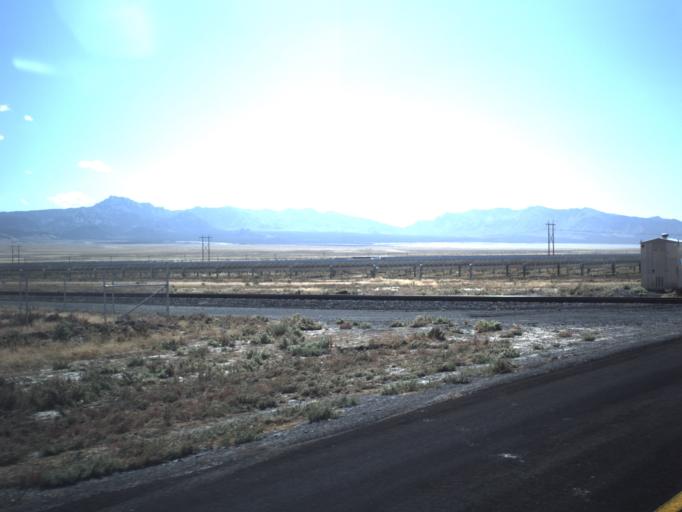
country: US
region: Utah
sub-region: Beaver County
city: Milford
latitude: 38.4946
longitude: -112.9912
